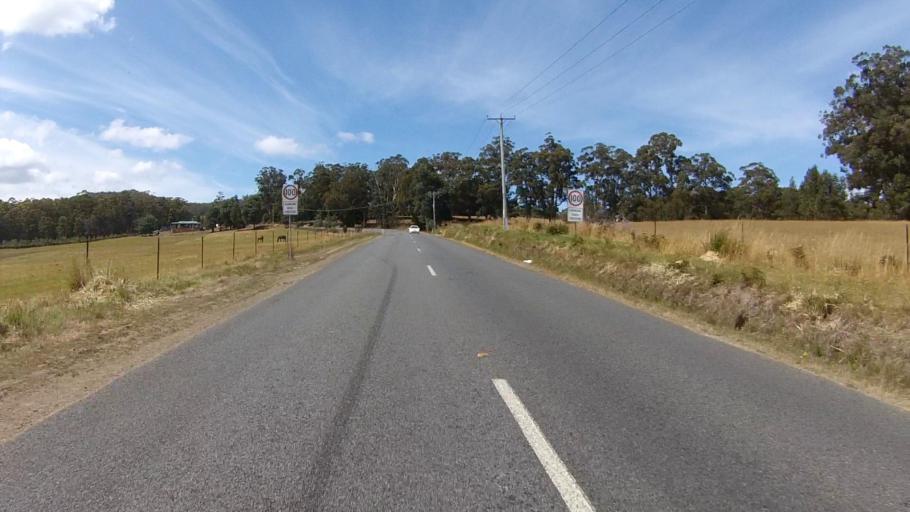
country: AU
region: Tasmania
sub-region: Huon Valley
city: Cygnet
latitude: -43.2124
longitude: 147.1167
